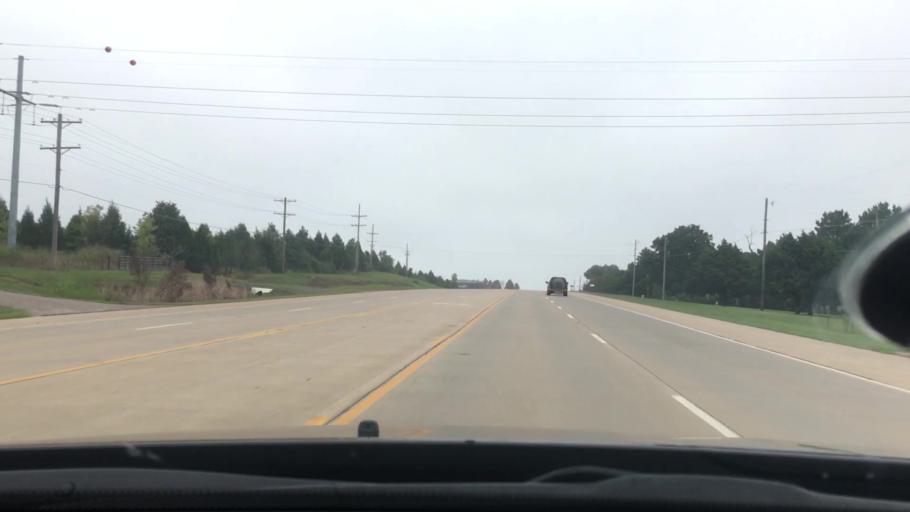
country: US
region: Oklahoma
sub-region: Seminole County
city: Seminole
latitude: 35.2639
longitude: -96.6710
